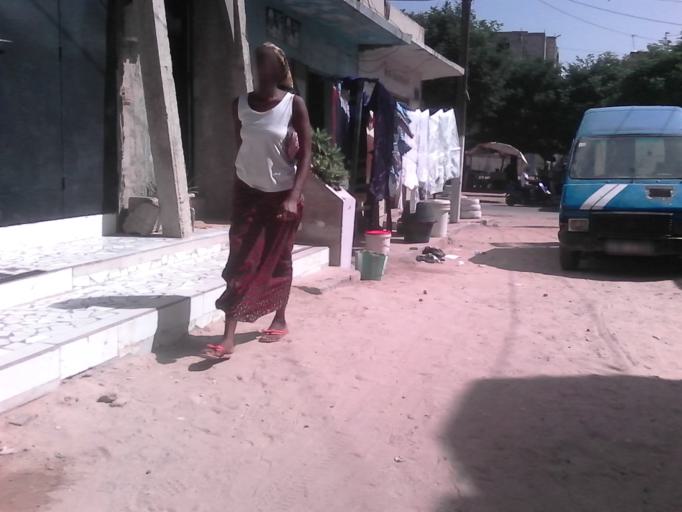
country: SN
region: Dakar
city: Grand Dakar
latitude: 14.7091
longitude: -17.4539
